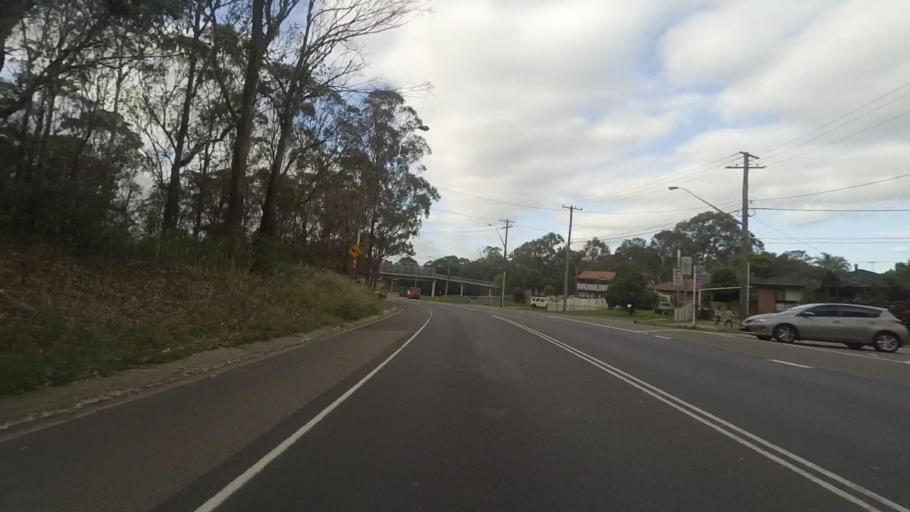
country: AU
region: New South Wales
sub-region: Bankstown
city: Milperra
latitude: -33.9093
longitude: 150.9814
